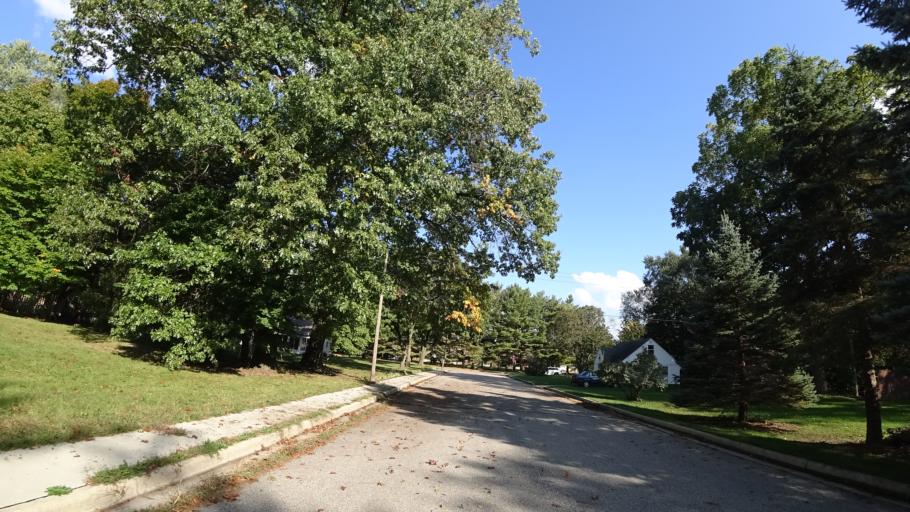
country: US
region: Michigan
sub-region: Saint Joseph County
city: Three Rivers
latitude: 41.9569
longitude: -85.6371
